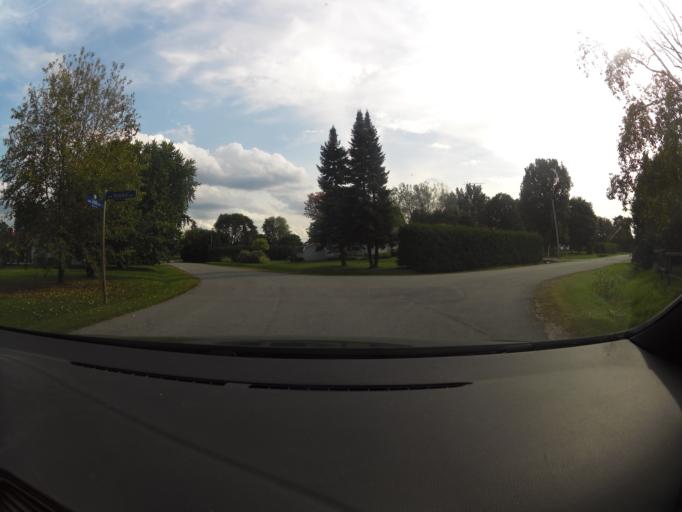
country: CA
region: Ontario
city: Carleton Place
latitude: 45.3599
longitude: -76.1204
